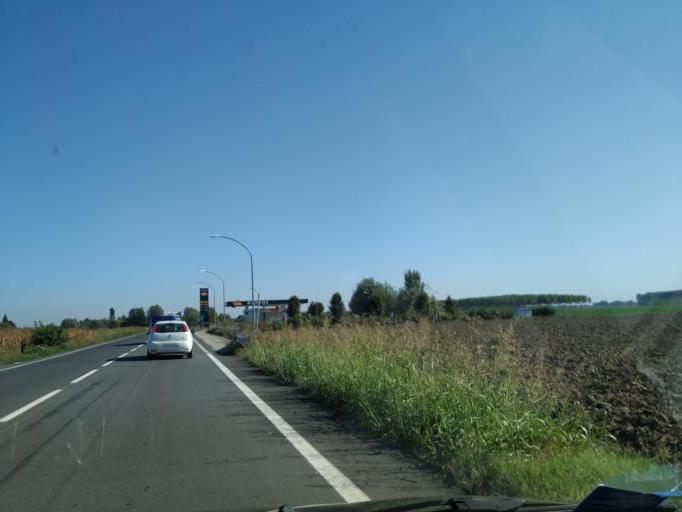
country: IT
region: Emilia-Romagna
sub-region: Provincia di Bologna
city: Decima
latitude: 44.7107
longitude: 11.2423
